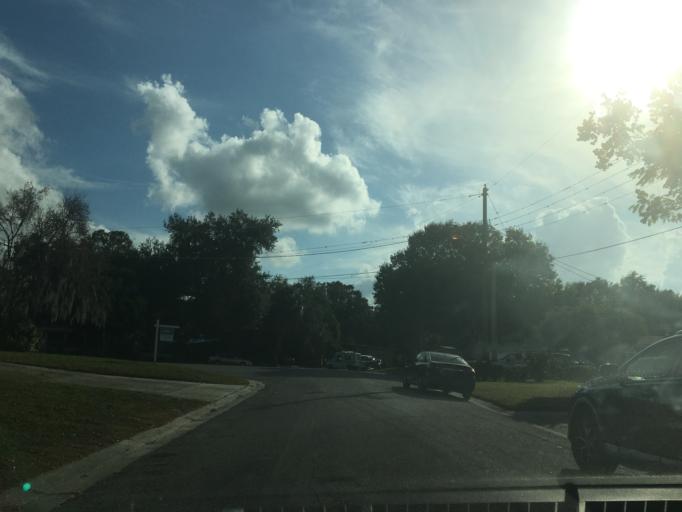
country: US
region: Florida
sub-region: Hillsborough County
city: Temple Terrace
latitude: 28.0080
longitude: -82.4160
